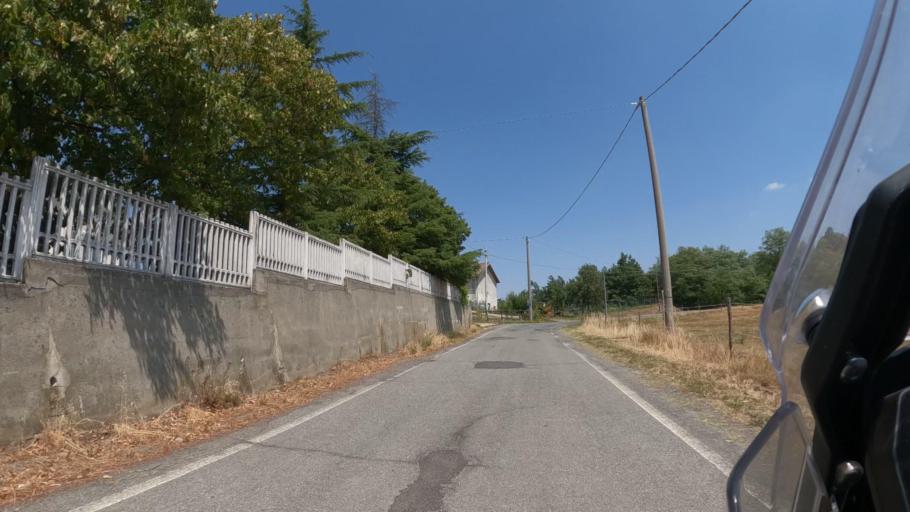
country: IT
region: Piedmont
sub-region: Provincia di Alessandria
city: Morbello
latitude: 44.5727
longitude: 8.5198
